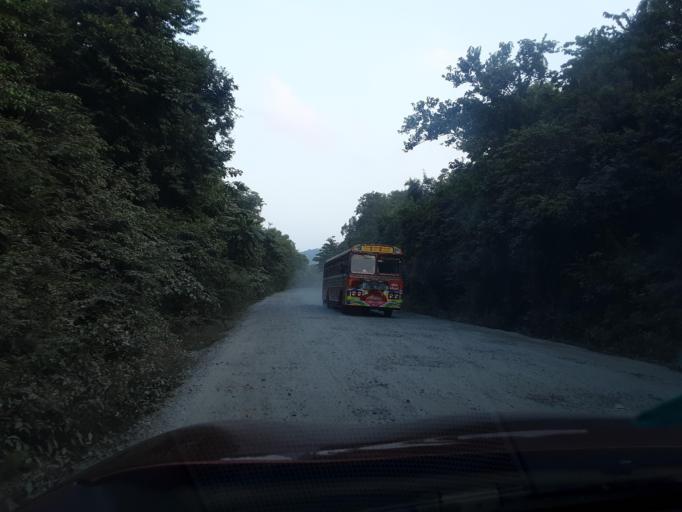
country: LK
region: Central
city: Dambulla
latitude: 7.8099
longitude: 80.7797
